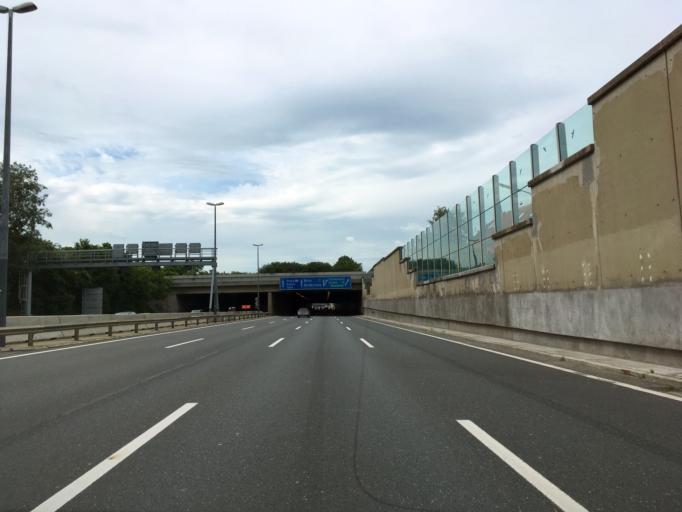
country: AT
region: Vienna
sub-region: Wien Stadt
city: Vienna
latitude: 48.2437
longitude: 16.3984
